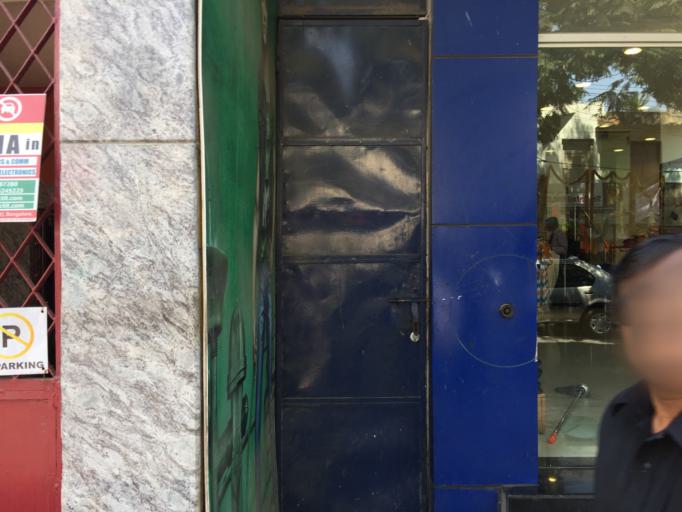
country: IN
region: Karnataka
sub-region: Bangalore Urban
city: Bangalore
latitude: 12.9723
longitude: 77.6504
